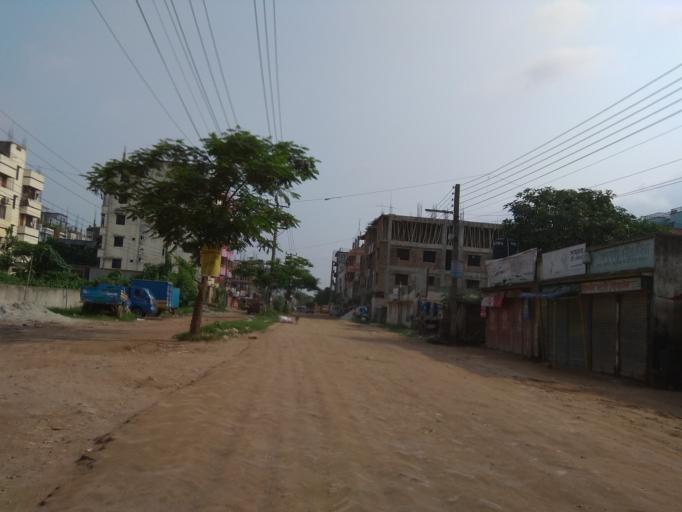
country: BD
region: Dhaka
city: Tungi
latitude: 23.8250
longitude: 90.3534
